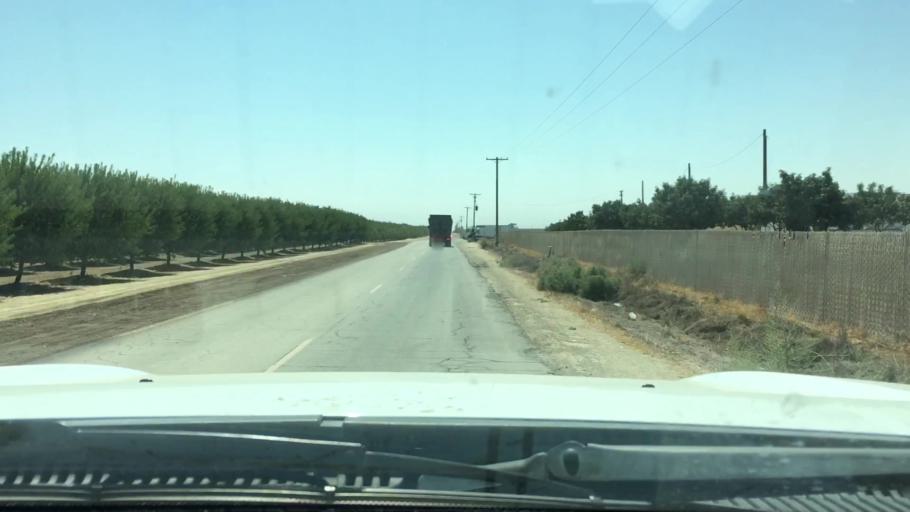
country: US
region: California
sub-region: Kern County
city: Wasco
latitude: 35.5161
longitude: -119.4033
